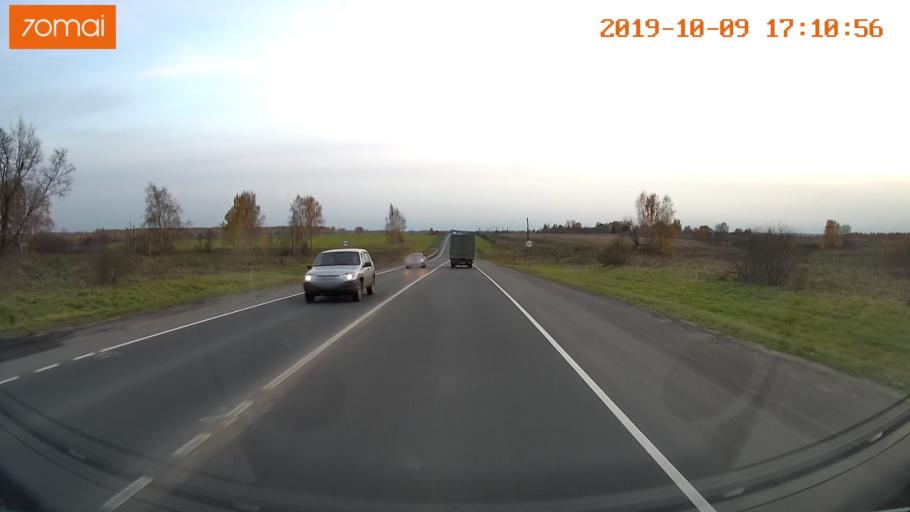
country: RU
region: Ivanovo
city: Privolzhsk
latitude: 57.3491
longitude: 41.2536
